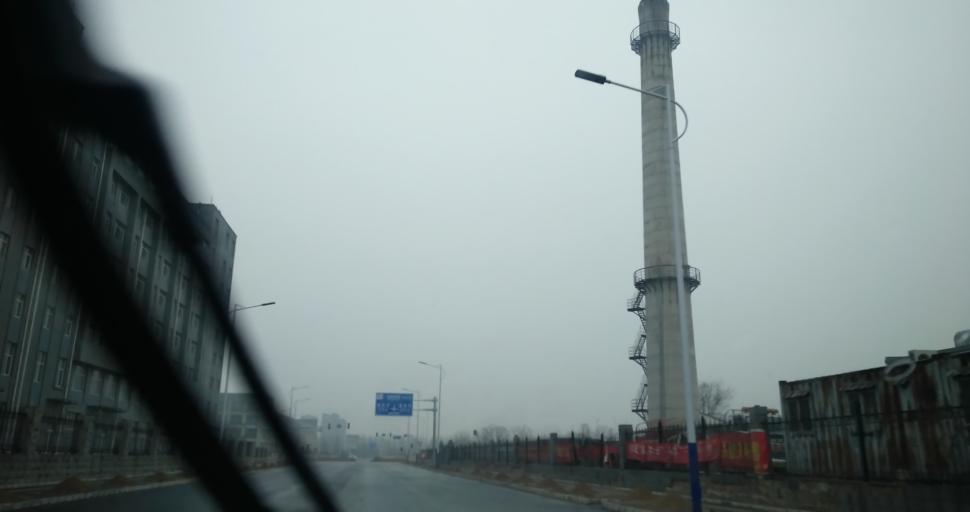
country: CN
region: Beijing
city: Yinghai
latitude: 39.7110
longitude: 116.4095
